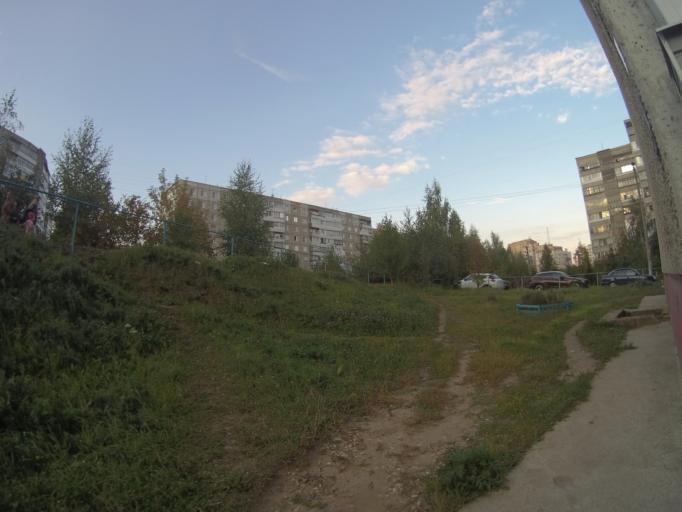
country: RU
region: Vladimir
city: Vladimir
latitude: 56.1062
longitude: 40.3530
